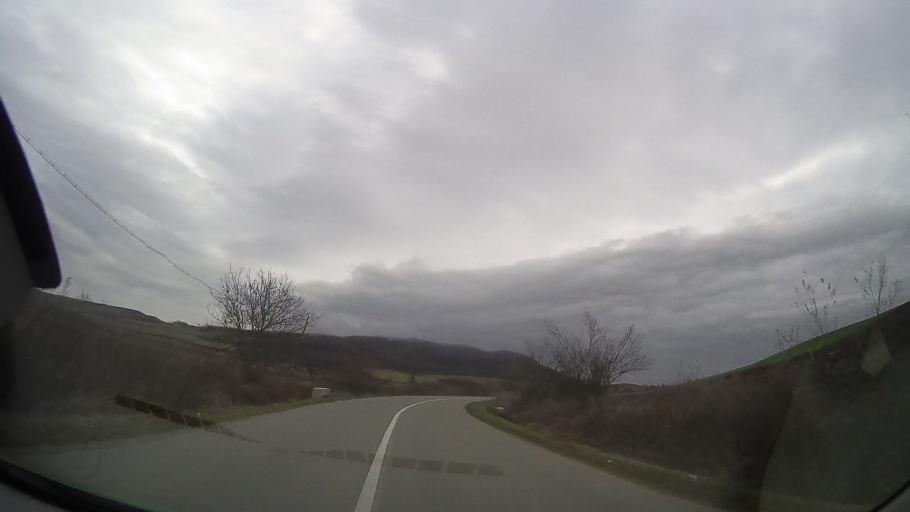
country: RO
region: Bistrita-Nasaud
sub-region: Comuna Milas
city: Milas
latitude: 46.8022
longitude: 24.4275
